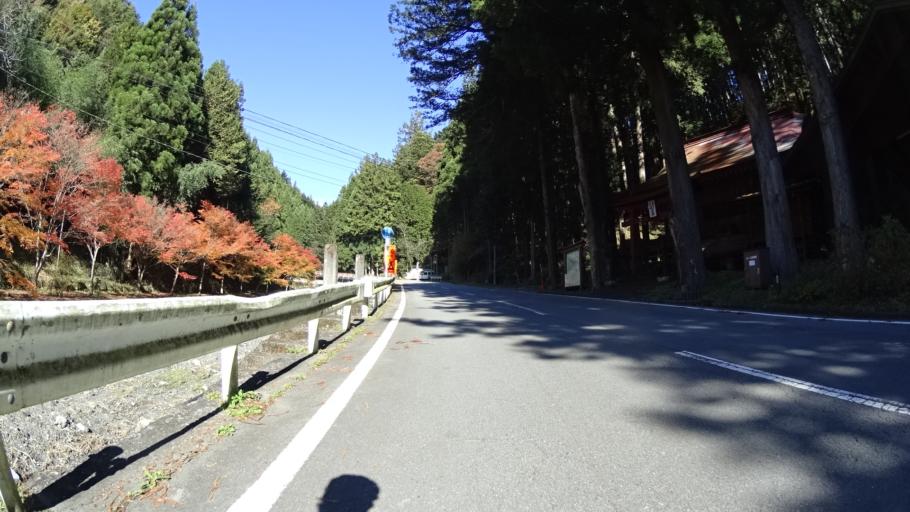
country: JP
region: Yamanashi
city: Otsuki
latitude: 35.7617
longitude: 138.9384
